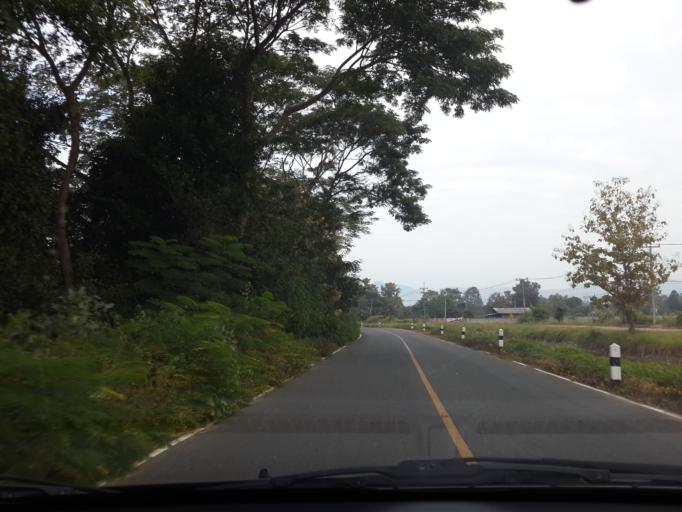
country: TH
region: Chiang Mai
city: San Sai
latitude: 18.8887
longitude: 99.0815
